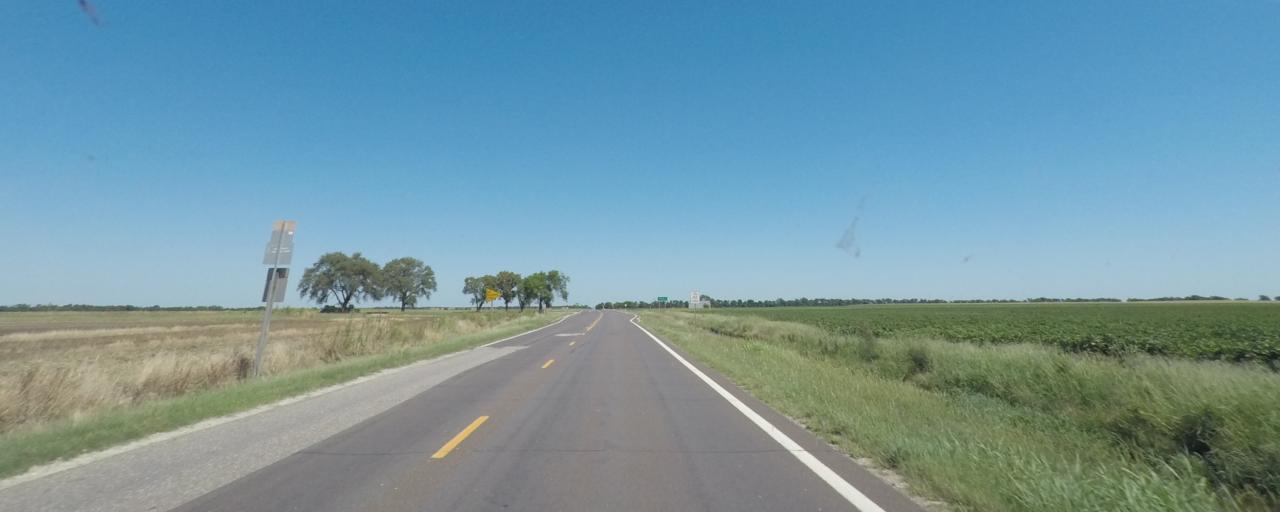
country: US
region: Kansas
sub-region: Sumner County
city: Wellington
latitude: 37.1714
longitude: -97.4019
